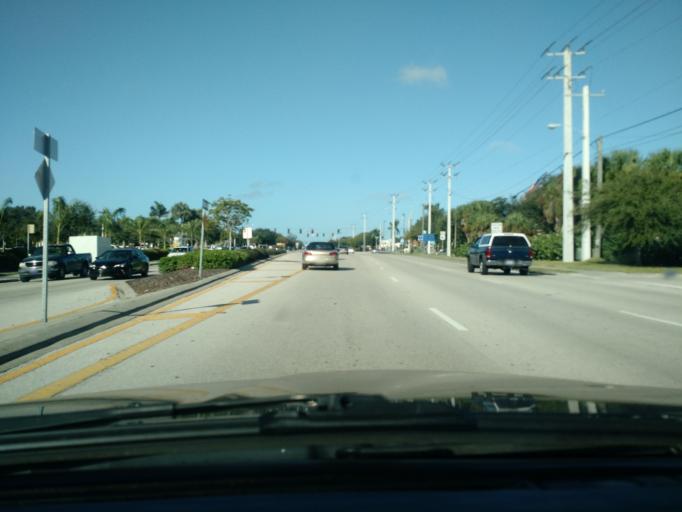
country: US
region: Florida
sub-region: Lee County
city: Bonita Springs
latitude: 26.3307
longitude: -81.8038
